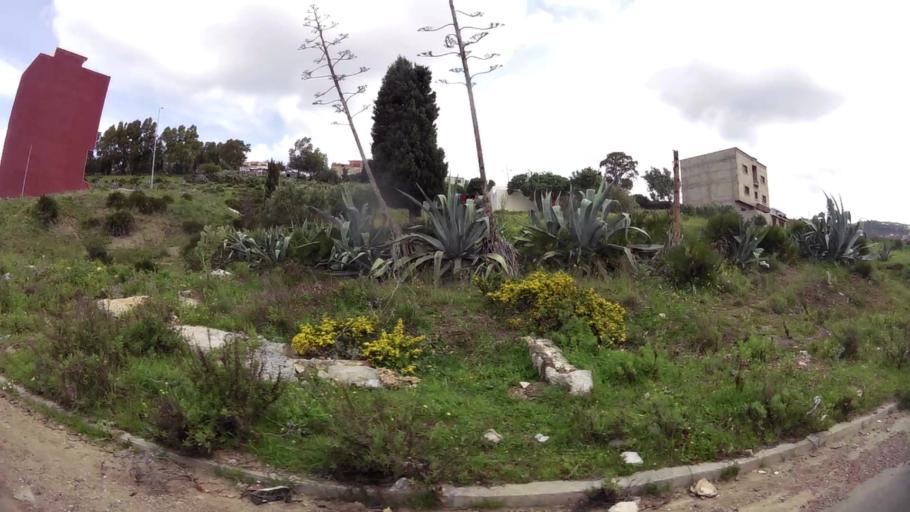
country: MA
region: Tanger-Tetouan
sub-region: Tanger-Assilah
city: Tangier
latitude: 35.7697
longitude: -5.7535
